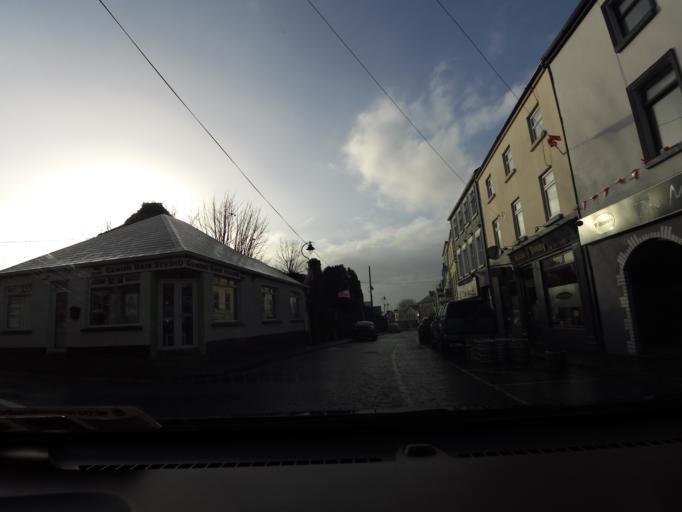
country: IE
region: Connaught
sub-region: County Galway
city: Tuam
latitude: 53.5147
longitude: -8.8523
